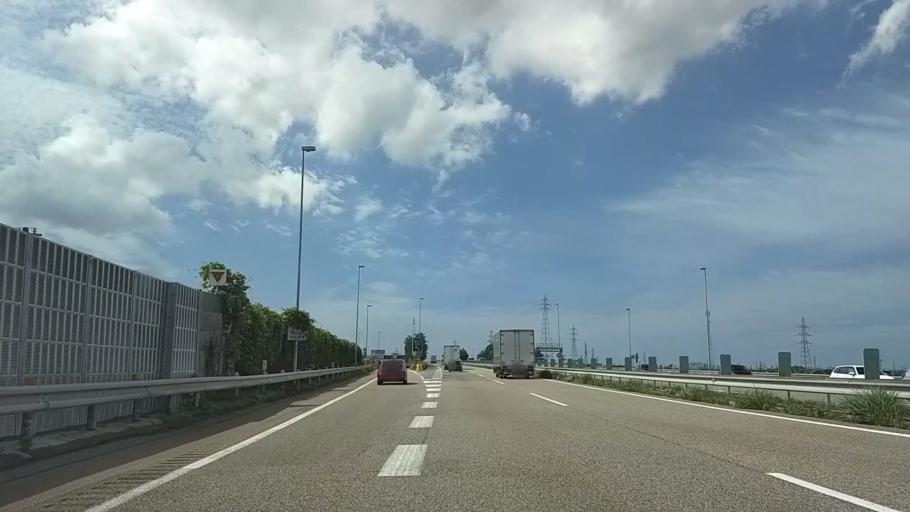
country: JP
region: Ishikawa
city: Kanazawa-shi
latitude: 36.6082
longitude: 136.6802
